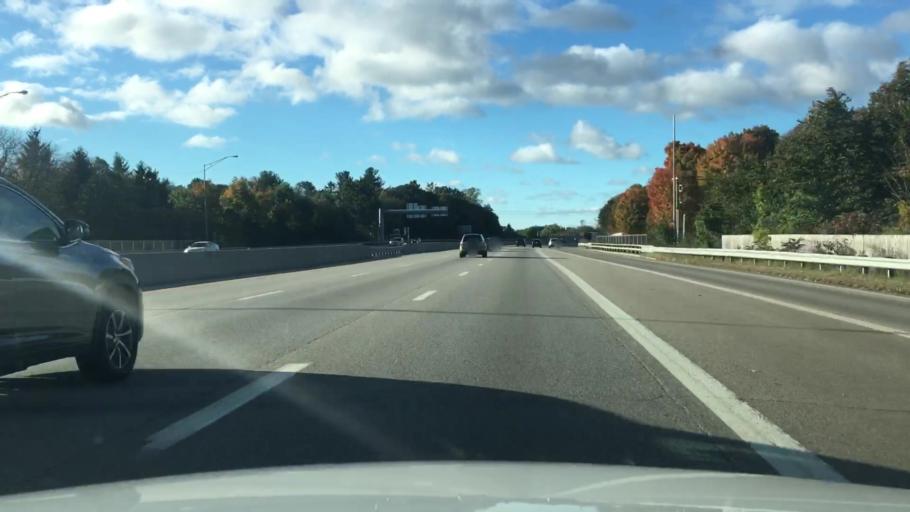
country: US
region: New Hampshire
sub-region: Rockingham County
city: Portsmouth
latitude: 43.0818
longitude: -70.7747
